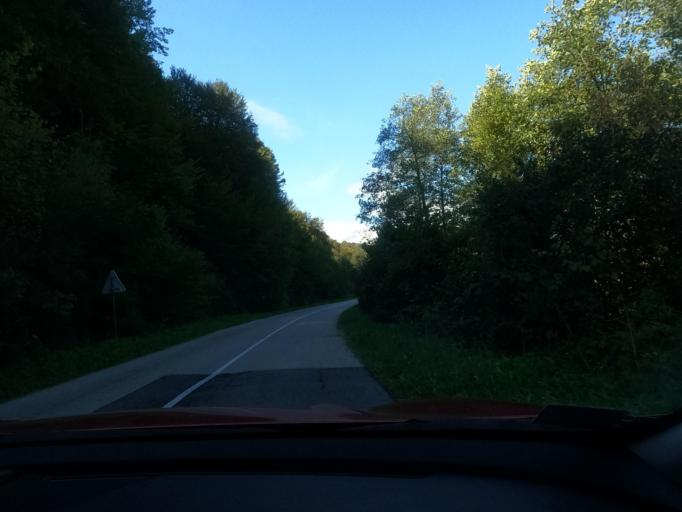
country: BA
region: Federation of Bosnia and Herzegovina
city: Vrnograc
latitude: 45.2638
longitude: 15.9685
